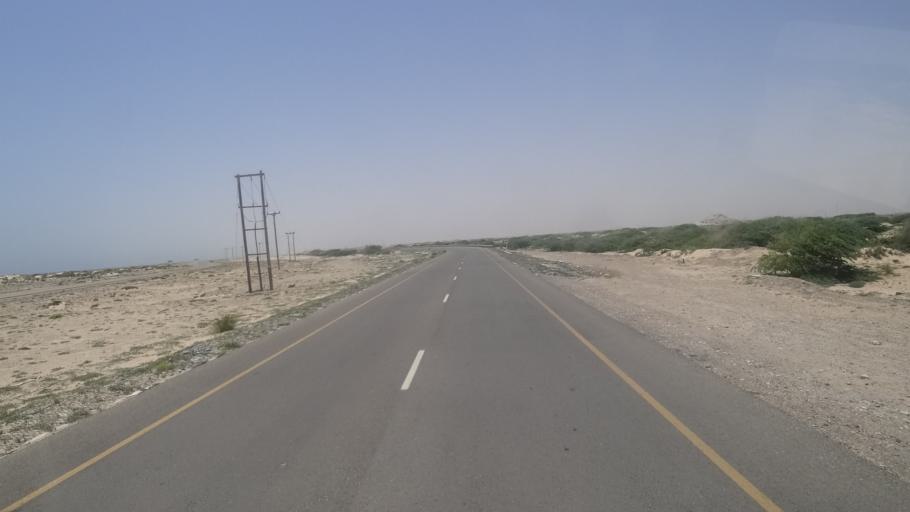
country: OM
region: Ash Sharqiyah
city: Sur
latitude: 22.0982
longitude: 59.6998
